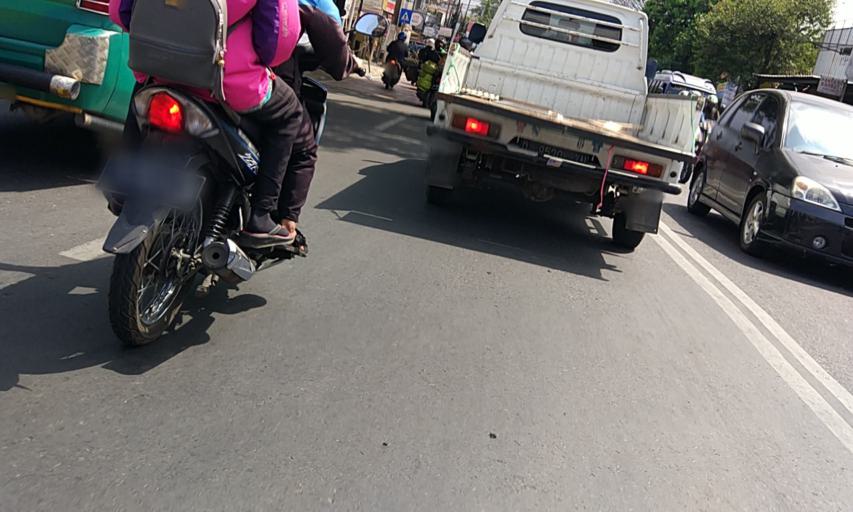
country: ID
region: West Java
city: Bandung
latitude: -6.9052
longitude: 107.6810
